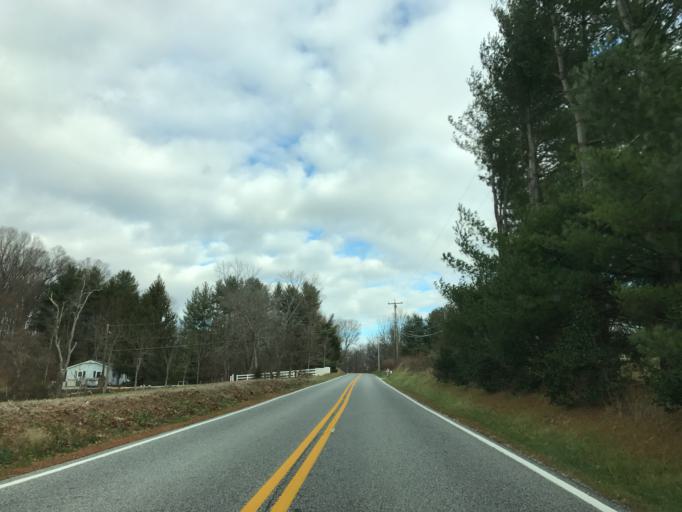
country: US
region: Pennsylvania
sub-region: York County
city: Stewartstown
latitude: 39.6395
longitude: -76.6294
